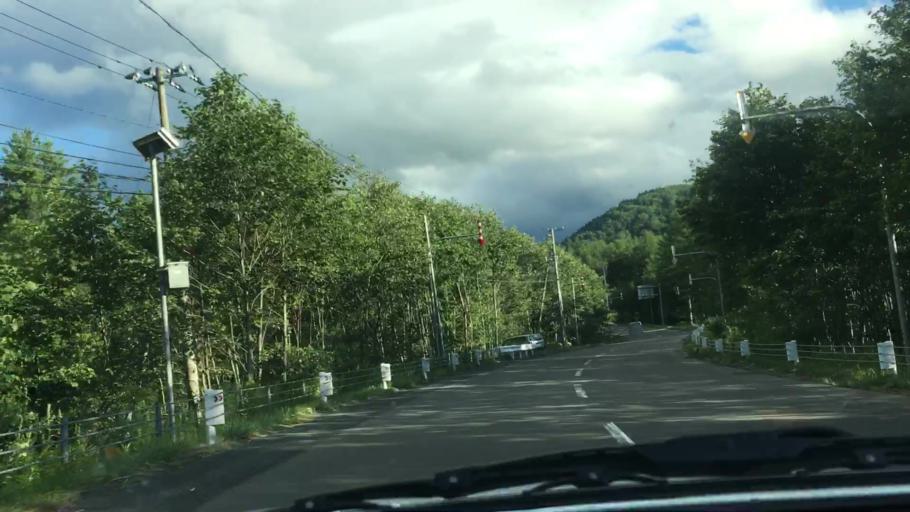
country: JP
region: Hokkaido
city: Shimo-furano
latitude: 43.1217
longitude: 142.6804
